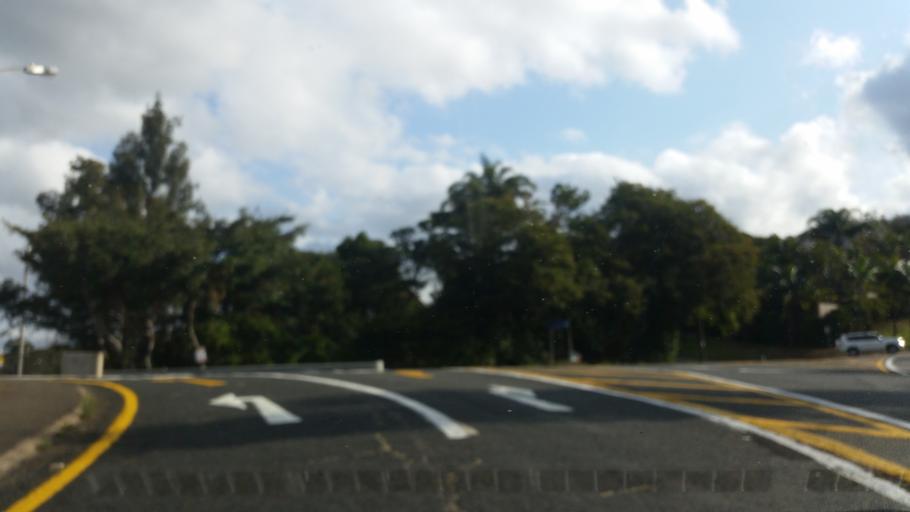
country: ZA
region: KwaZulu-Natal
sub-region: eThekwini Metropolitan Municipality
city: Berea
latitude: -29.8313
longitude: 30.9410
